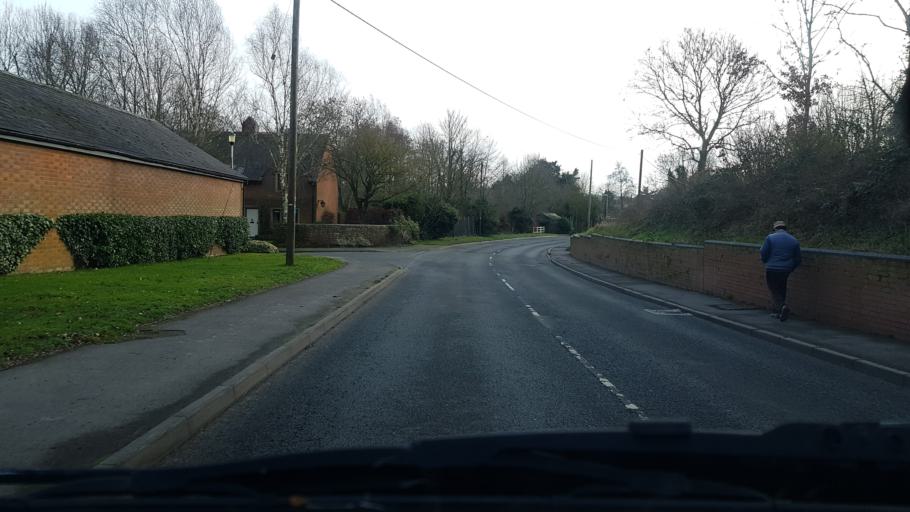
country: GB
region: England
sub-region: Wiltshire
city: Pewsey
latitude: 51.3372
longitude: -1.7674
